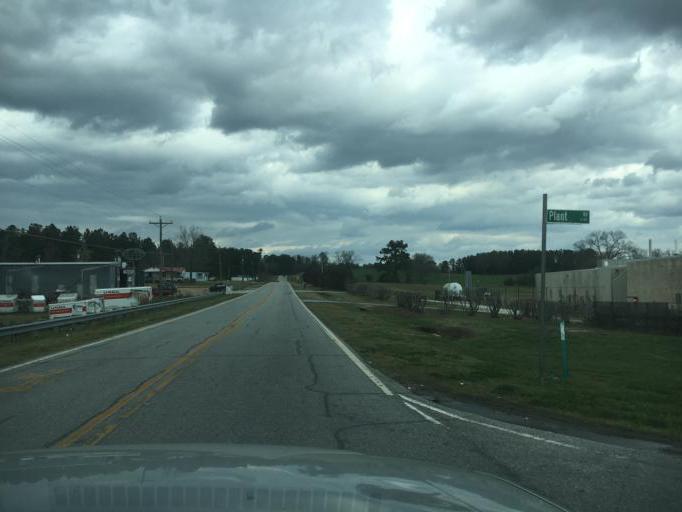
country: US
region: South Carolina
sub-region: Oconee County
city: Westminster
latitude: 34.6911
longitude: -83.0813
